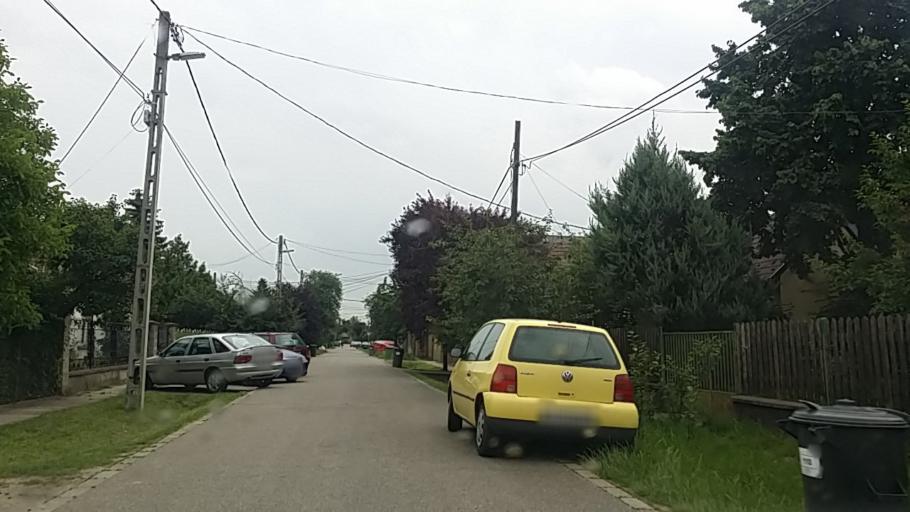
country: HU
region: Pest
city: Vecses
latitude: 47.4028
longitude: 19.2603
